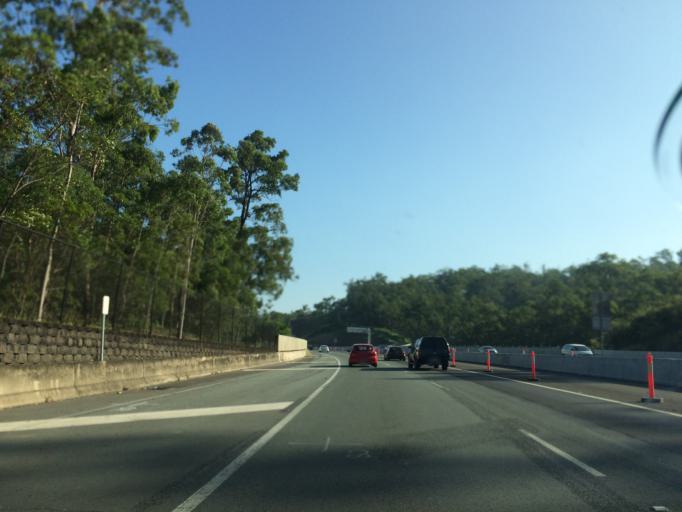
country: AU
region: Queensland
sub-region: Brisbane
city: Taringa
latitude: -27.4839
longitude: 152.9680
